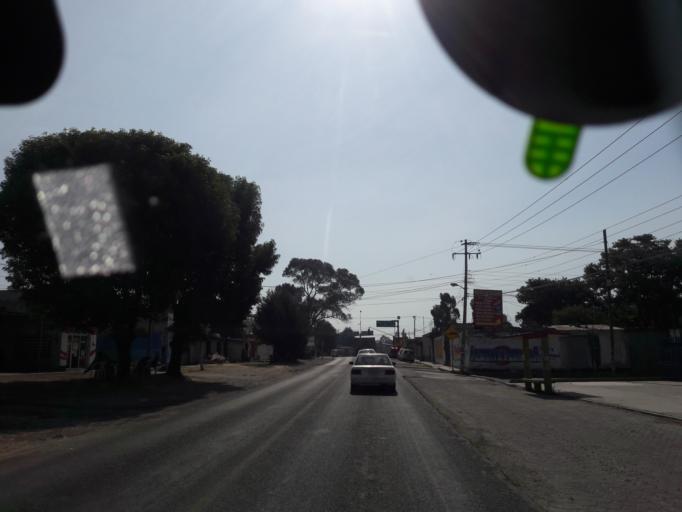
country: MX
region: Tlaxcala
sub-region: Panotla
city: Fraccionamiento la Virgen
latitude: 19.3192
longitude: -98.2736
